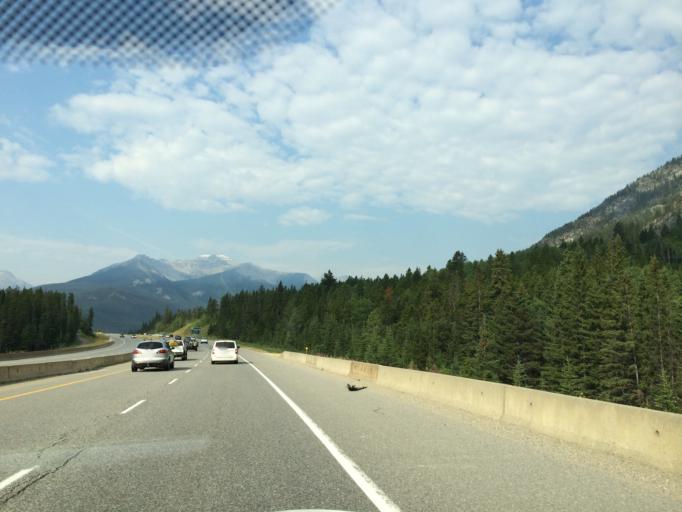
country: CA
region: Alberta
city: Banff
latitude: 51.1753
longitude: -115.6450
